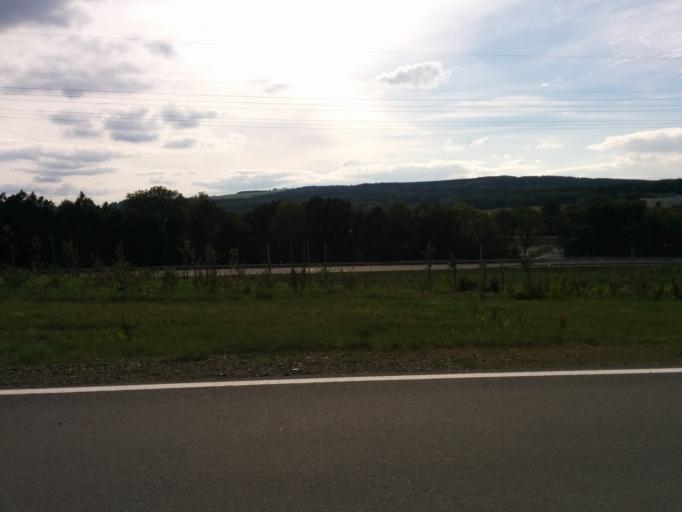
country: DE
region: Saxony
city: Floha
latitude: 50.8504
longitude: 13.0845
